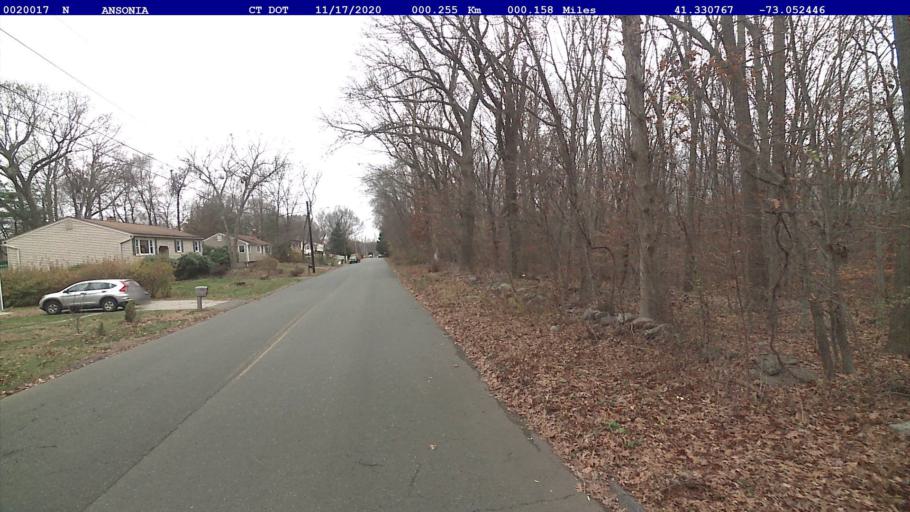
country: US
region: Connecticut
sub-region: New Haven County
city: Ansonia
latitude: 41.3308
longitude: -73.0525
